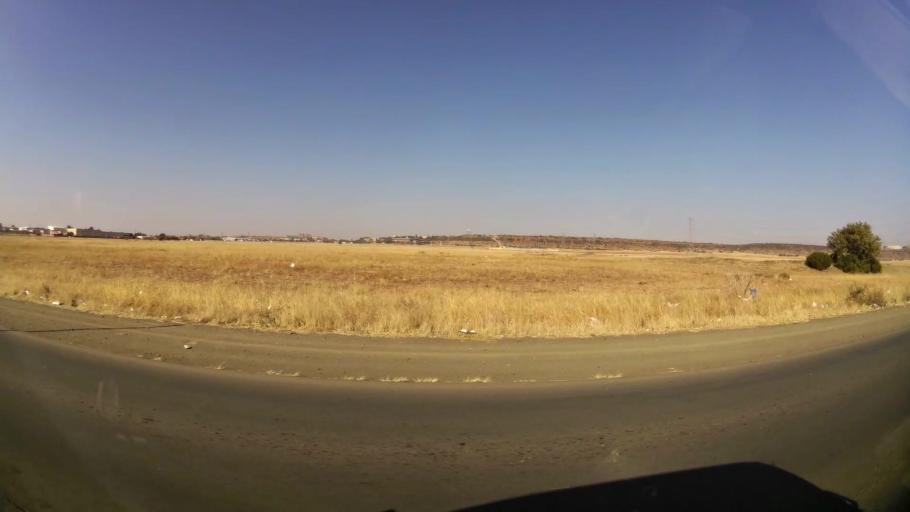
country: ZA
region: Orange Free State
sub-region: Mangaung Metropolitan Municipality
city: Bloemfontein
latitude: -29.1718
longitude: 26.2154
